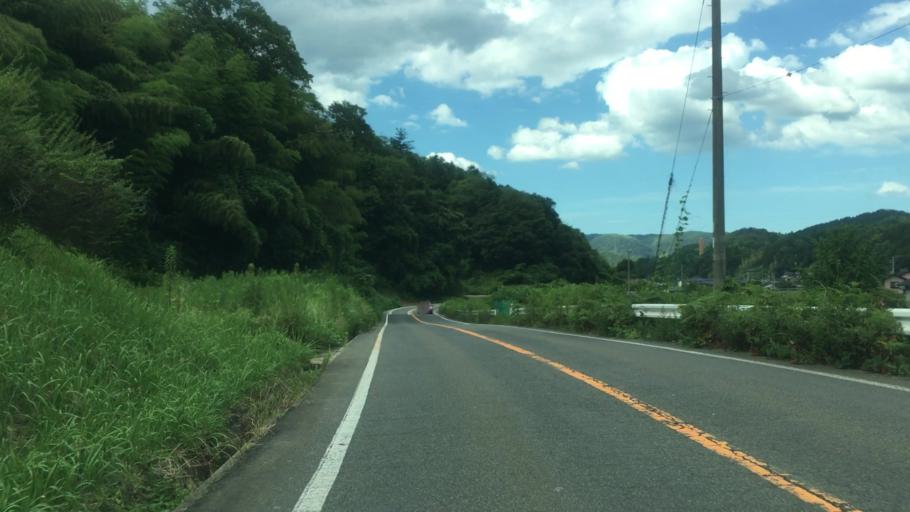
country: JP
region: Hyogo
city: Toyooka
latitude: 35.5332
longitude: 134.7886
